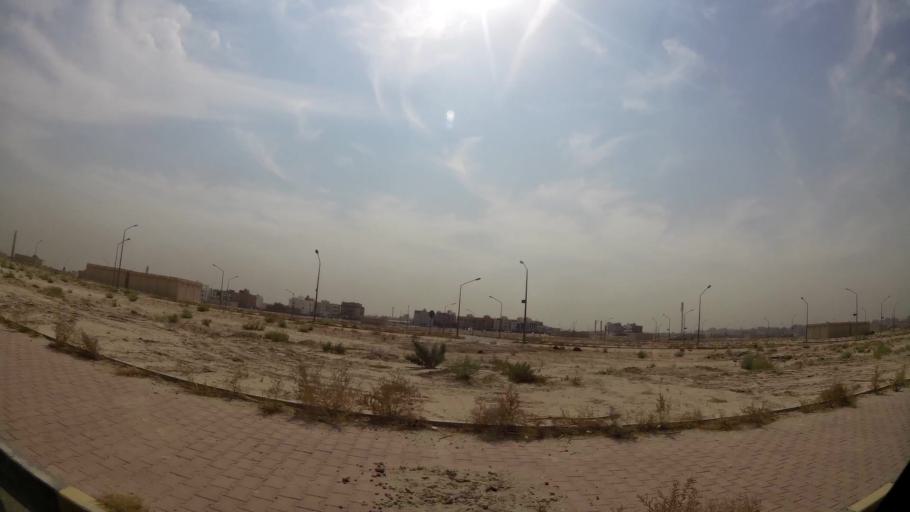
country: KW
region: Al Farwaniyah
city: Janub as Surrah
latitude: 29.2993
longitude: 47.9887
